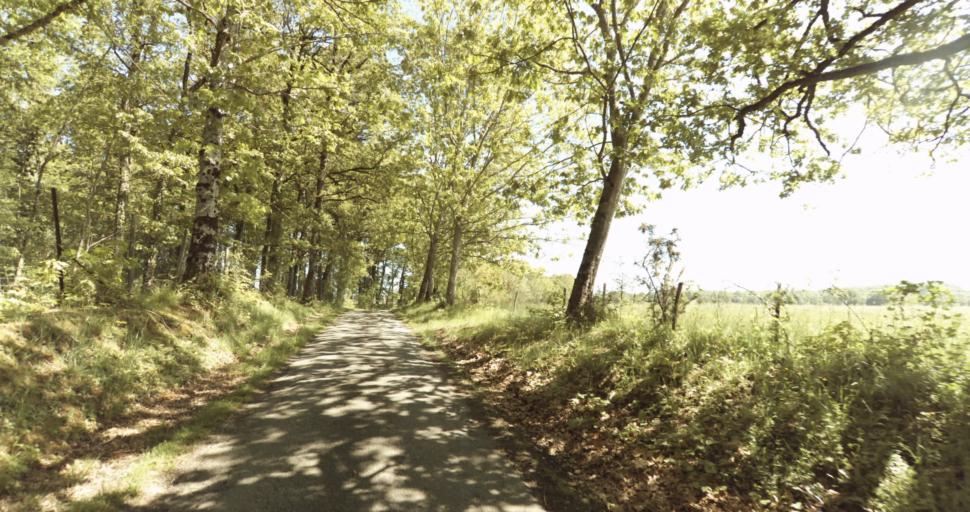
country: FR
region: Limousin
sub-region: Departement de la Haute-Vienne
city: Le Vigen
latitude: 45.7582
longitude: 1.3054
